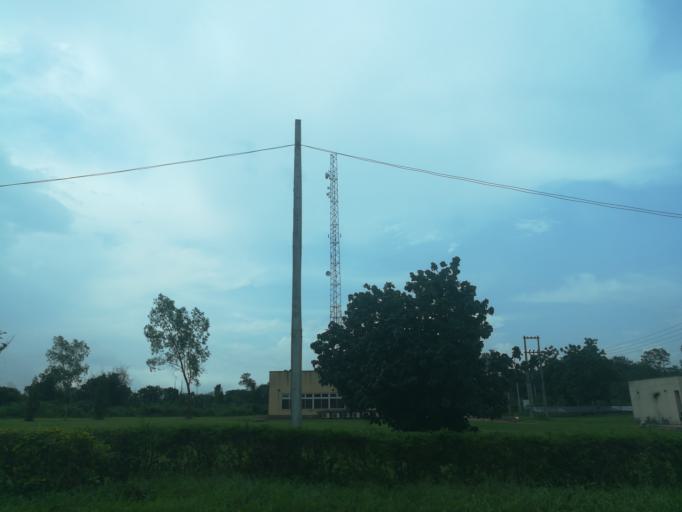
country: NG
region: Lagos
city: Ikorodu
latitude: 6.6417
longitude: 3.5228
